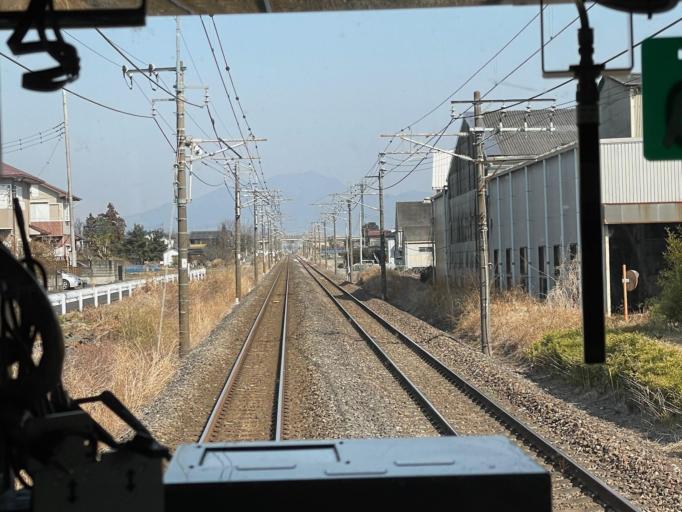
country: JP
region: Gunma
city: Kanekomachi
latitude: 36.4209
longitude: 139.0312
